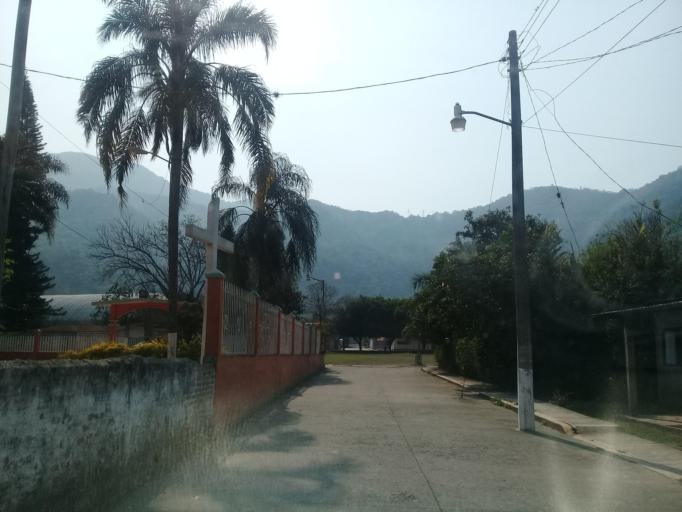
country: MX
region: Veracruz
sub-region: Ixtaczoquitlan
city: Campo Chico
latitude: 18.8374
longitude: -97.0283
